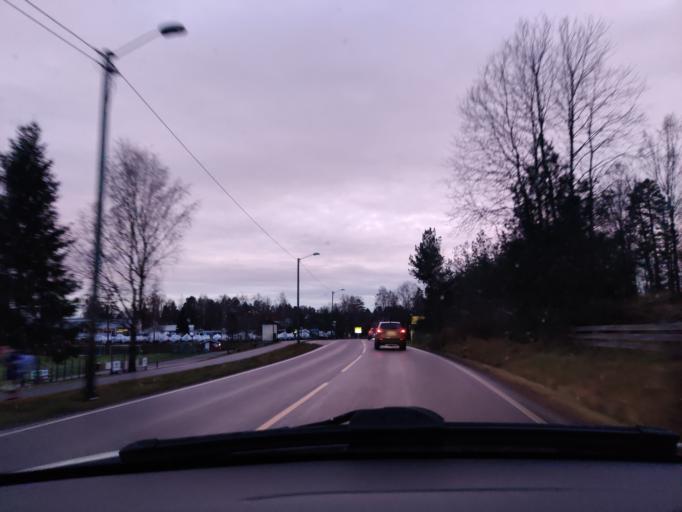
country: NO
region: Vestfold
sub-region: Stokke
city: Melsomvik
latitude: 59.2557
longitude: 10.3586
